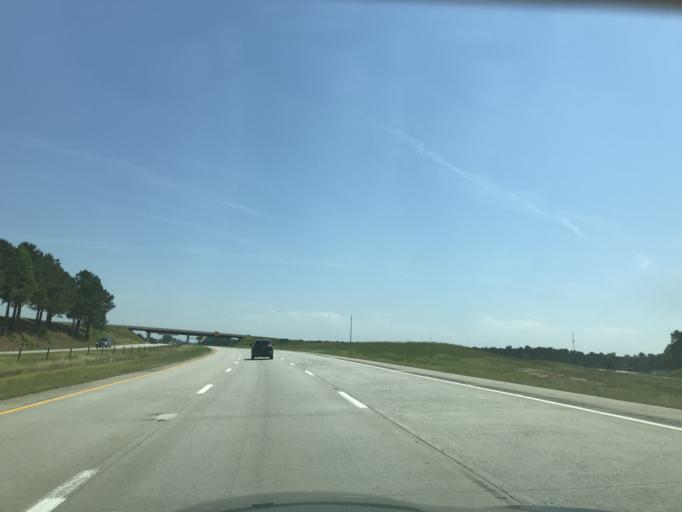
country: US
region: North Carolina
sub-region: Johnston County
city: Benson
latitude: 35.3936
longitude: -78.5213
